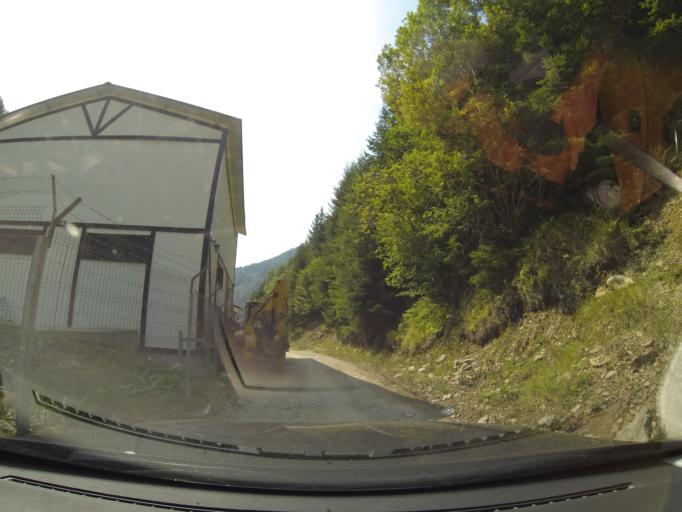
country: RO
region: Arges
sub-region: Comuna Arefu
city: Arefu
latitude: 45.4945
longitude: 24.6446
